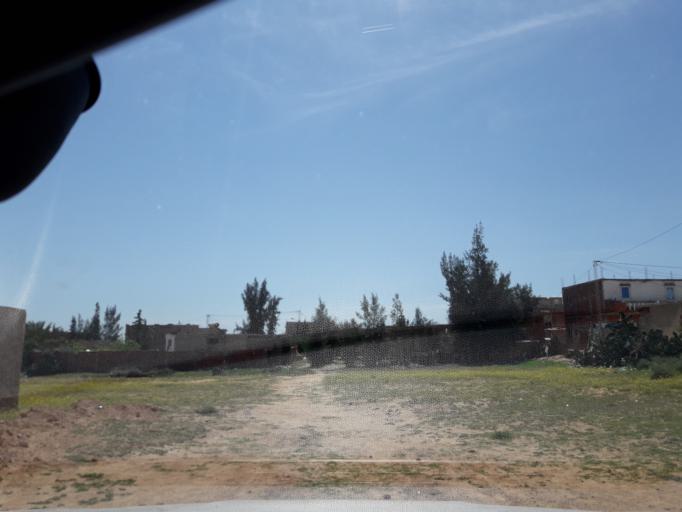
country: TN
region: Safaqis
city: Sfax
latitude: 34.7454
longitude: 10.5134
